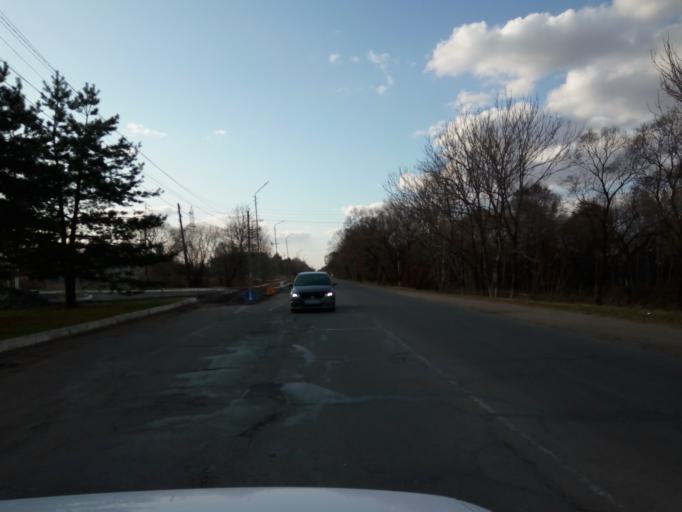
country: RU
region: Primorskiy
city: Dal'nerechensk
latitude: 45.9179
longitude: 133.7619
